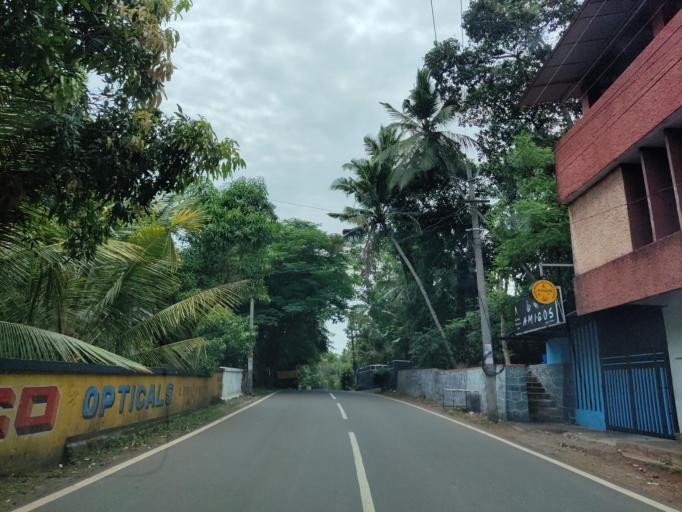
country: IN
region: Kerala
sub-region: Alappuzha
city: Chengannur
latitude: 9.2828
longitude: 76.6145
